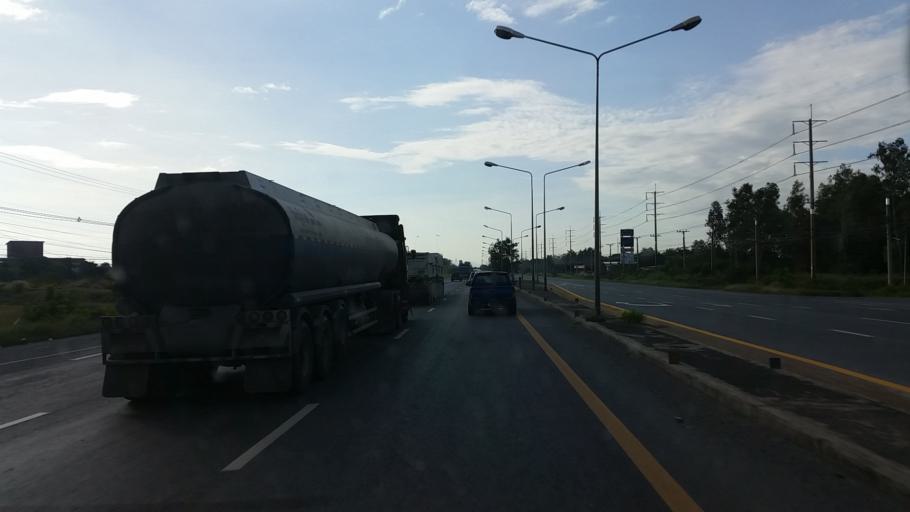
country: TH
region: Sara Buri
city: Chaloem Phra Kiat
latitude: 14.5971
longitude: 100.8968
